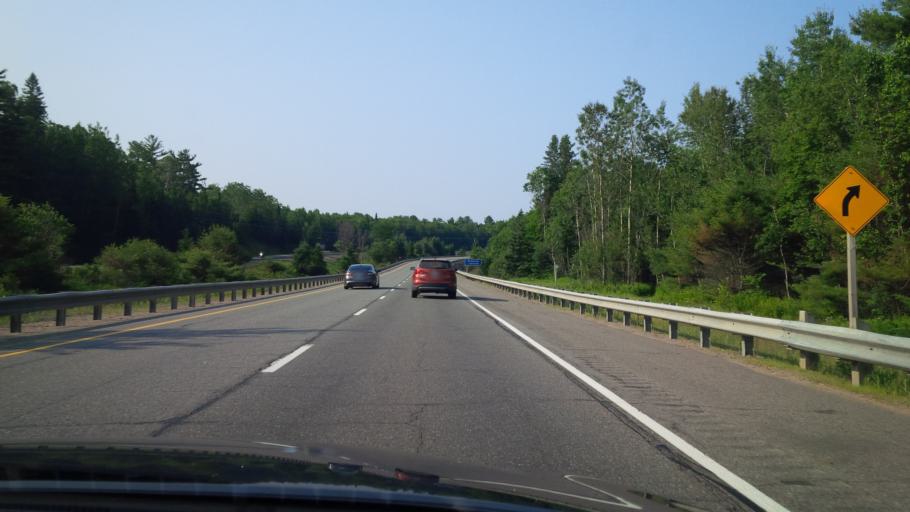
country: CA
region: Ontario
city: Huntsville
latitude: 45.3601
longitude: -79.2196
